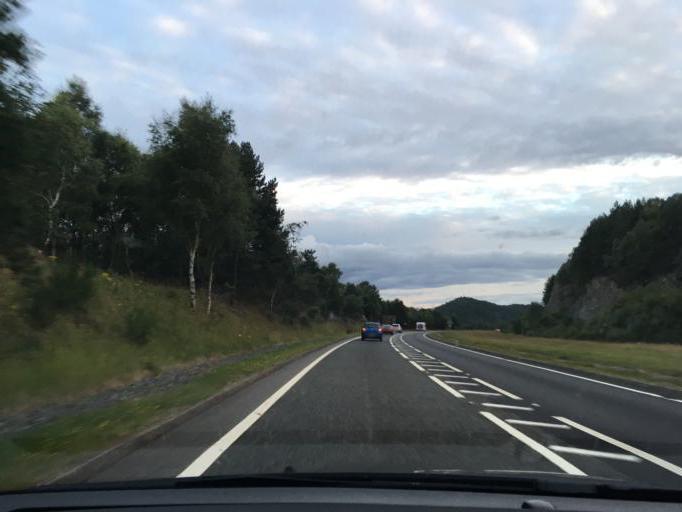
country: GB
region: Scotland
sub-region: Highland
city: Aviemore
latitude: 57.1789
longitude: -3.8358
